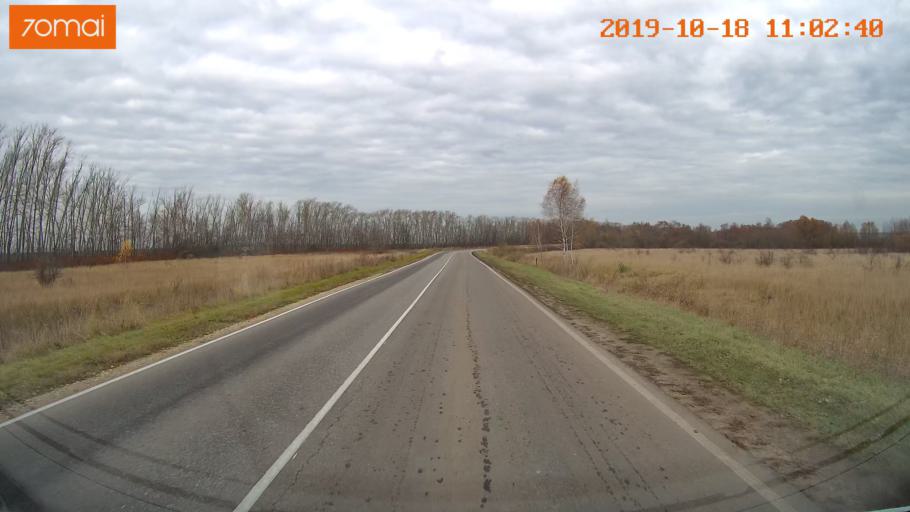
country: RU
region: Tula
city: Yepifan'
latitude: 53.8690
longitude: 38.5436
